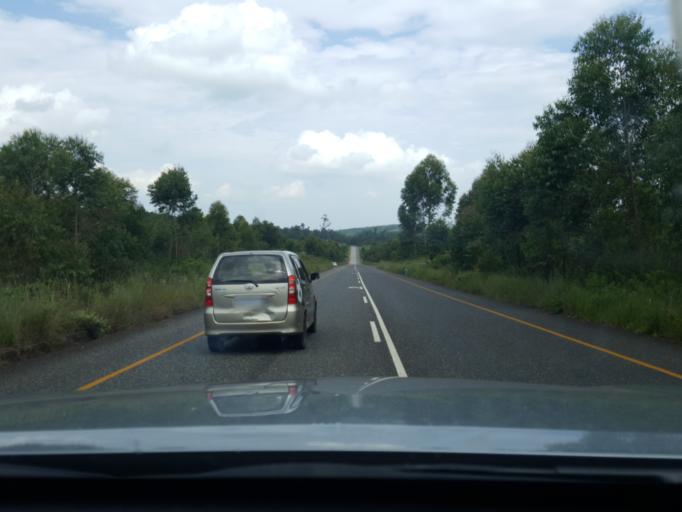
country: ZA
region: Mpumalanga
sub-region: Ehlanzeni District
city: White River
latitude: -25.1776
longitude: 30.8747
